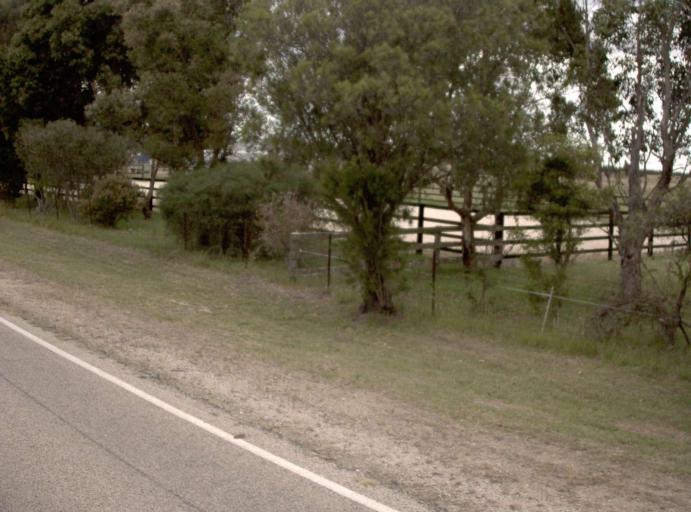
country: AU
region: Victoria
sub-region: East Gippsland
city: Bairnsdale
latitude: -37.8670
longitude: 147.5620
